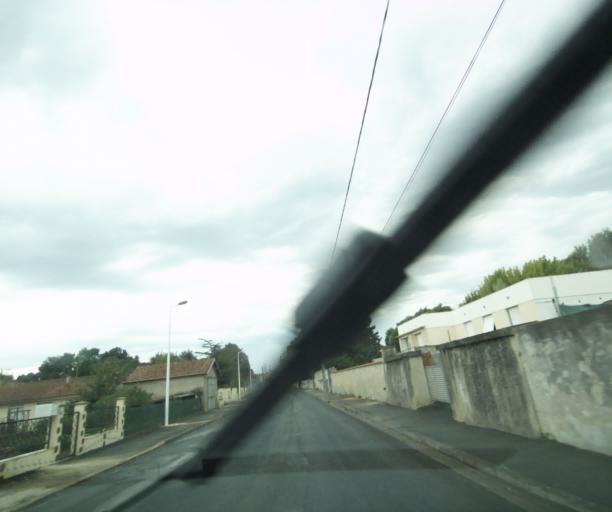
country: FR
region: Poitou-Charentes
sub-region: Departement de la Charente-Maritime
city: Tonnay-Charente
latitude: 45.9470
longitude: -0.8811
